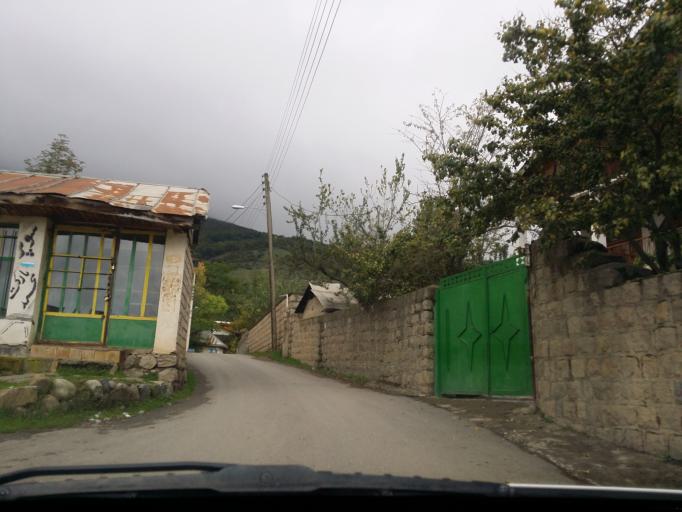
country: IR
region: Mazandaran
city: `Abbasabad
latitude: 36.5046
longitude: 51.1867
